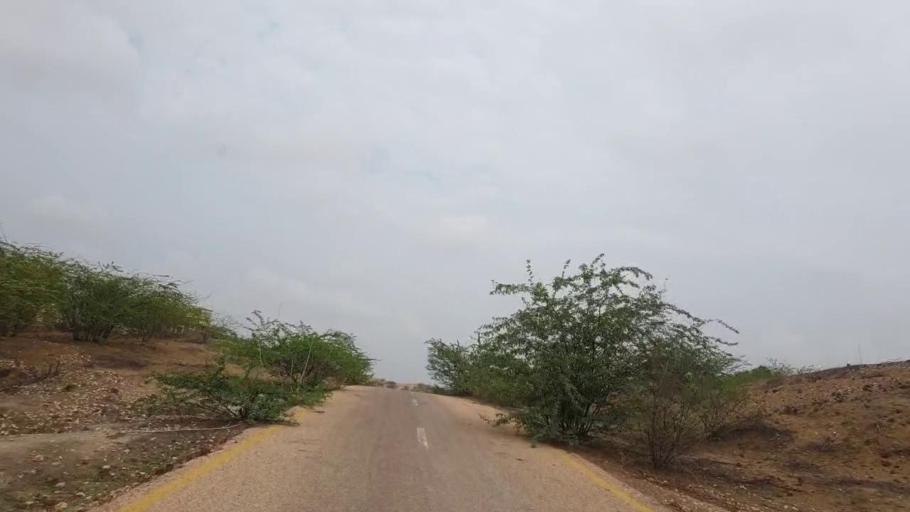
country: PK
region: Sindh
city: Naukot
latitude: 24.6242
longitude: 69.3704
